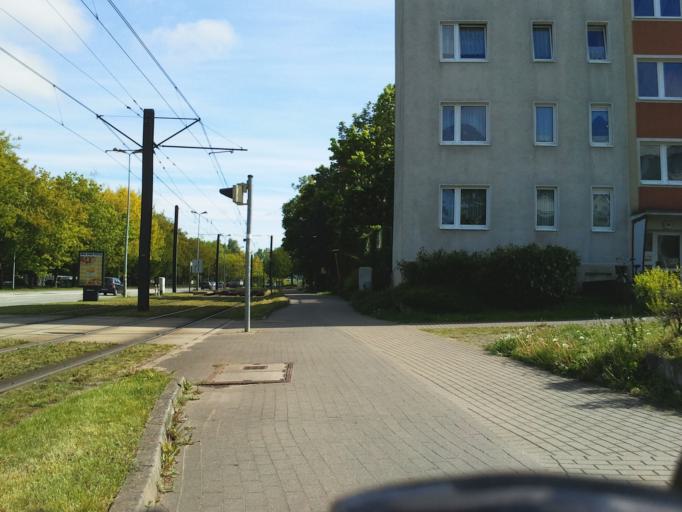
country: DE
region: Mecklenburg-Vorpommern
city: Rostock
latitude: 54.0675
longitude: 12.1165
